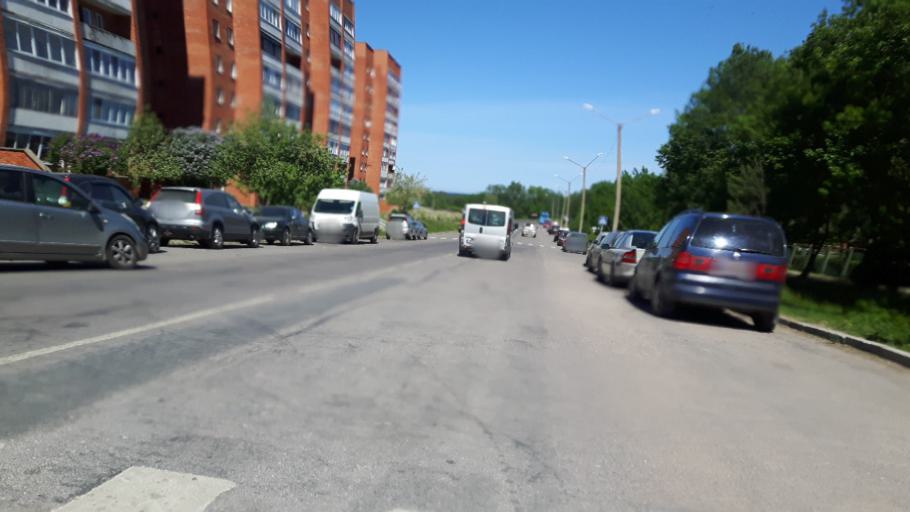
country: EE
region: Ida-Virumaa
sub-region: Sillamaee linn
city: Sillamae
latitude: 59.3919
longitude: 27.7970
